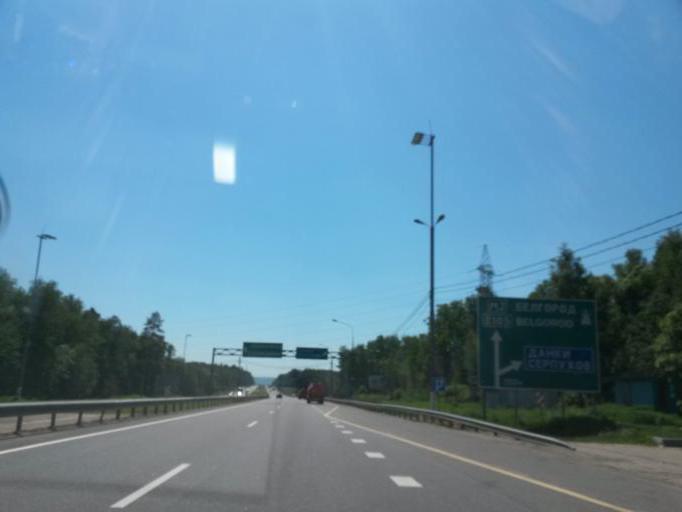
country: RU
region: Moskovskaya
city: Danki
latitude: 54.9109
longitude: 37.5117
